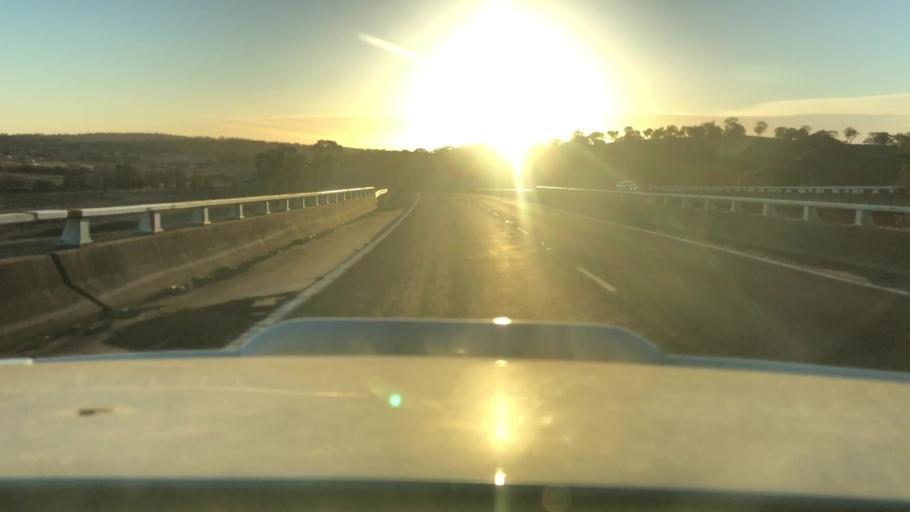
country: AU
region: New South Wales
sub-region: Goulburn Mulwaree
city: Goulburn
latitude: -34.7869
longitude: 149.6563
